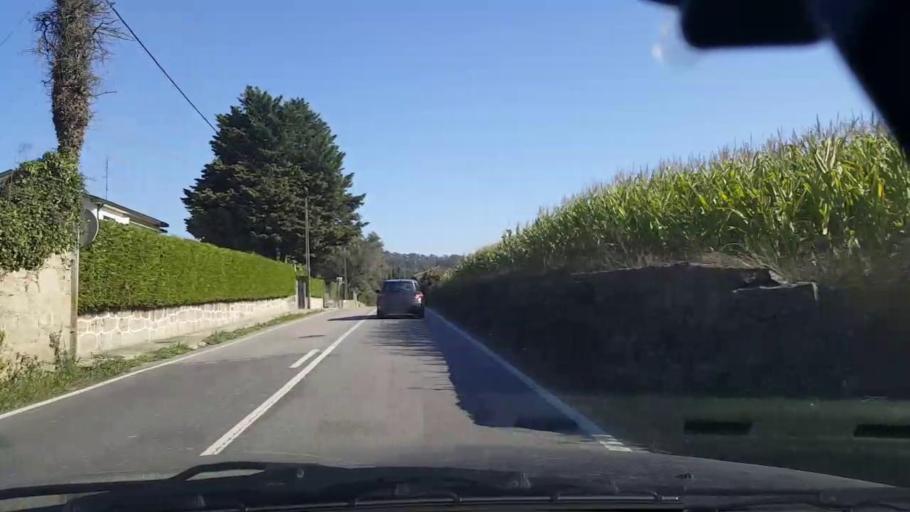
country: PT
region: Porto
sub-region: Vila do Conde
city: Arvore
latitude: 41.3292
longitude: -8.6602
